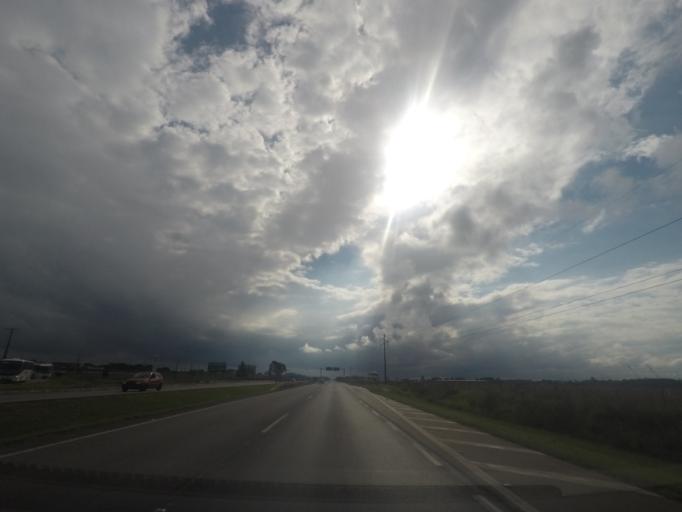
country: BR
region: Parana
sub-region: Piraquara
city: Piraquara
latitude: -25.5196
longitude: -49.1096
